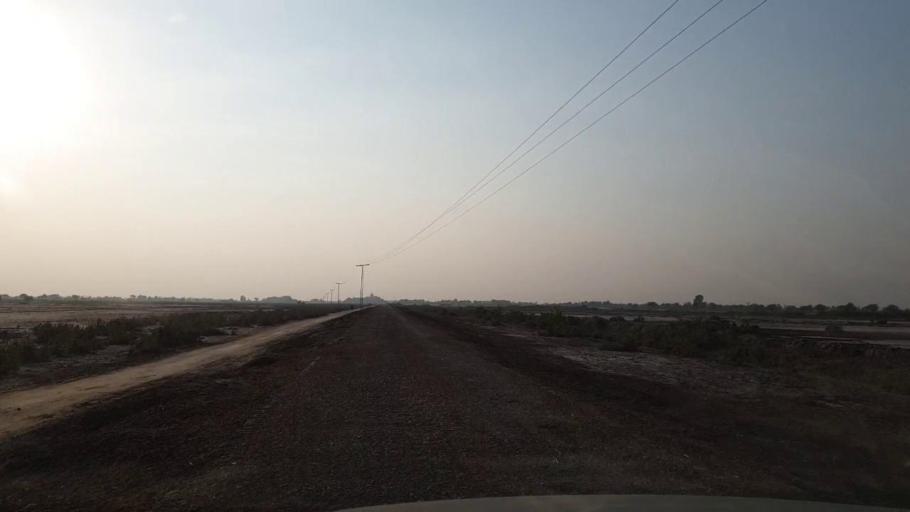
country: PK
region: Sindh
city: Pithoro
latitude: 25.6524
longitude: 69.2448
